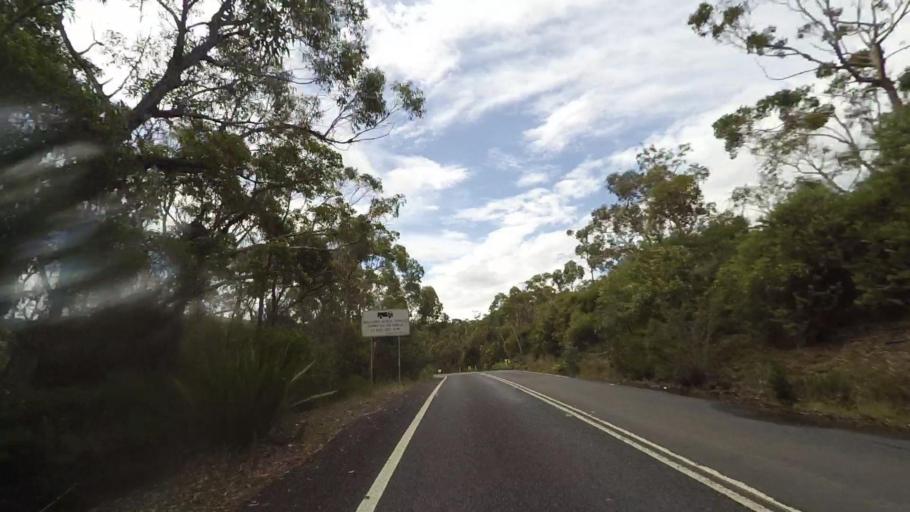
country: AU
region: New South Wales
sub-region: Sutherland Shire
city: Grays Point
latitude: -34.1158
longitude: 151.0692
